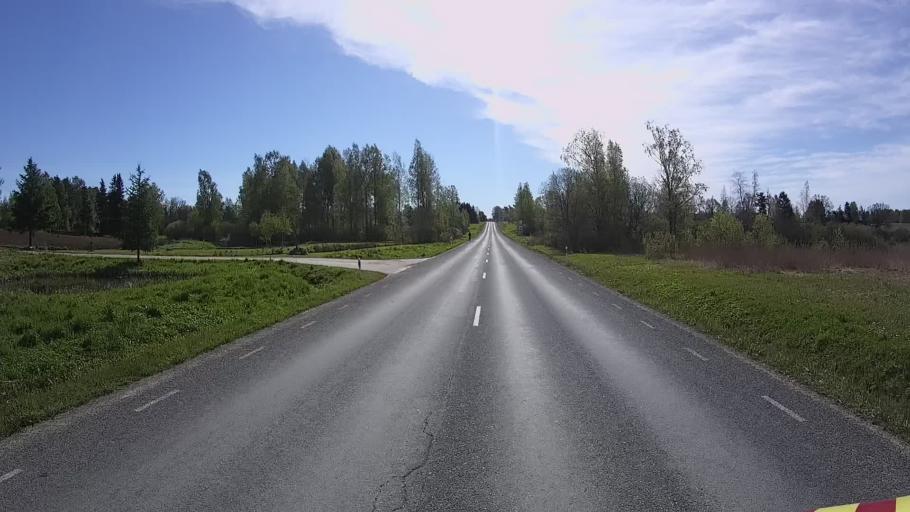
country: EE
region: Polvamaa
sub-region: Polva linn
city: Polva
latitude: 58.1576
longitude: 27.1725
